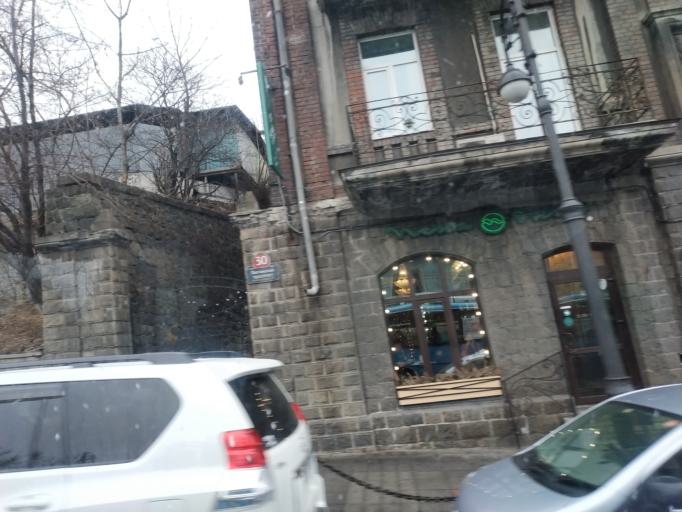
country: RU
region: Primorskiy
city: Vladivostok
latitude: 43.1214
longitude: 131.8876
